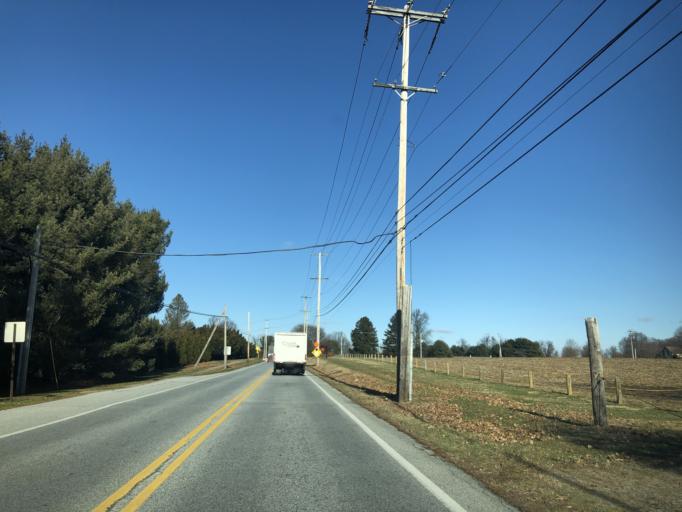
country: US
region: Pennsylvania
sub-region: Chester County
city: Kennett Square
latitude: 39.8893
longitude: -75.7220
